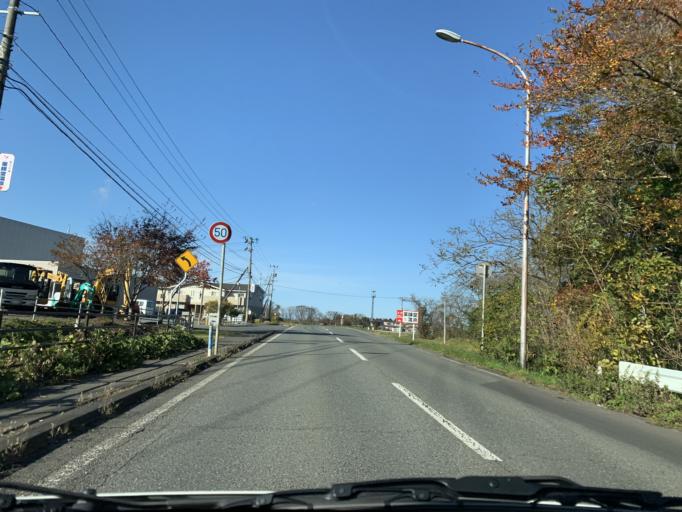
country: JP
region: Iwate
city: Mizusawa
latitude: 39.1724
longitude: 141.1408
